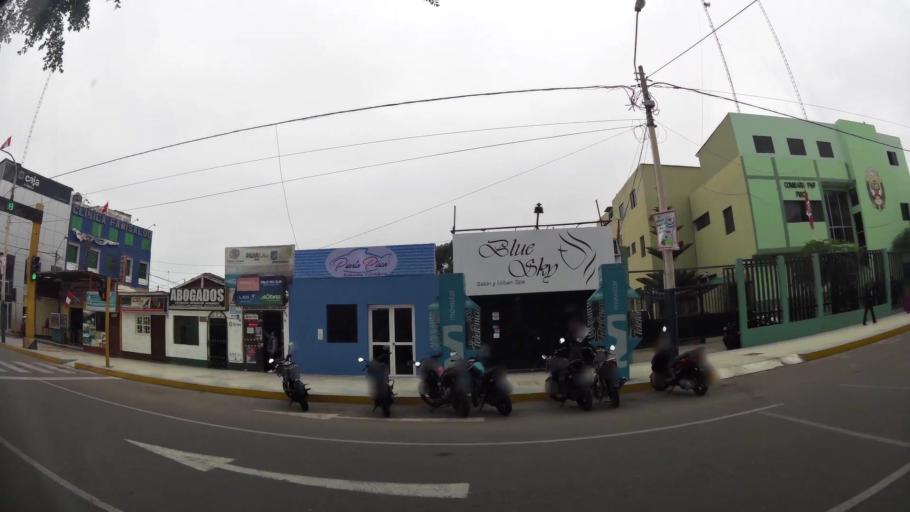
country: PE
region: Ica
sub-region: Provincia de Pisco
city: Pisco
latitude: -13.7095
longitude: -76.2033
